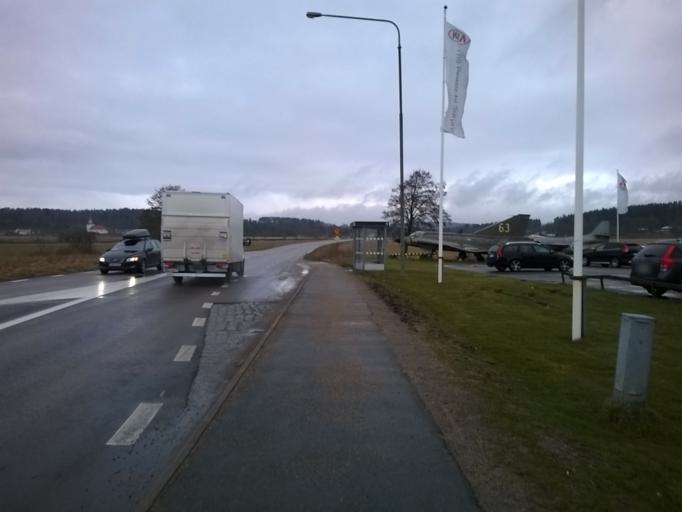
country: SE
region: Vaestra Goetaland
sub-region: Kungalvs Kommun
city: Kungalv
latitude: 57.9055
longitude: 11.9241
